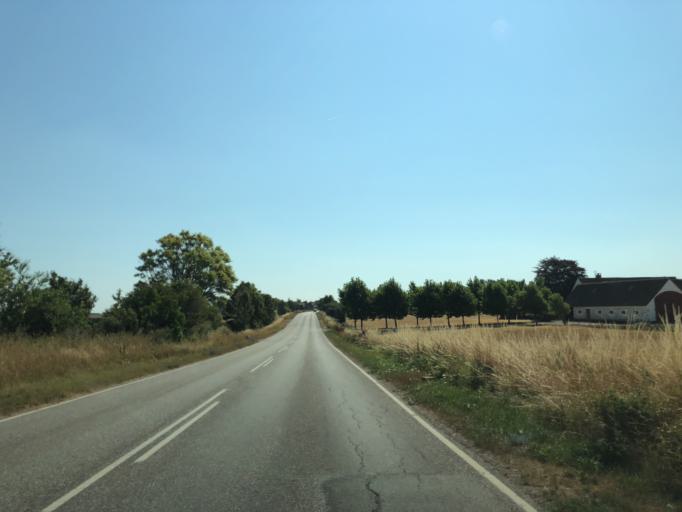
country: DK
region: Zealand
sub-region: Odsherred Kommune
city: Asnaes
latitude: 55.9636
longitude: 11.3769
